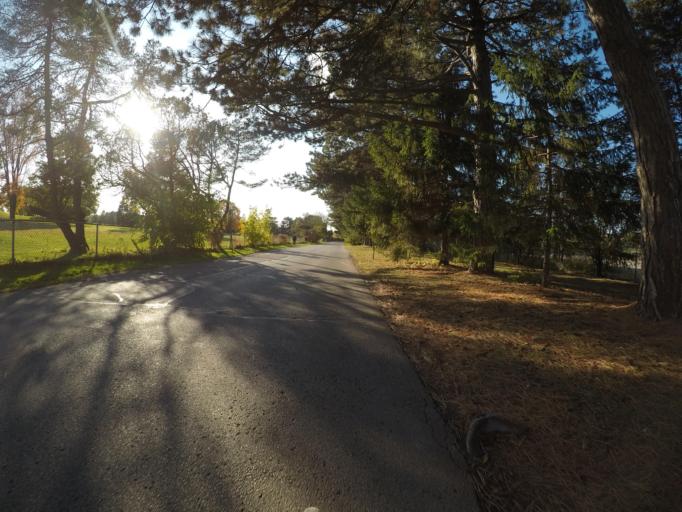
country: CA
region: Ontario
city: Kitchener
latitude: 43.4390
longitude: -80.4697
